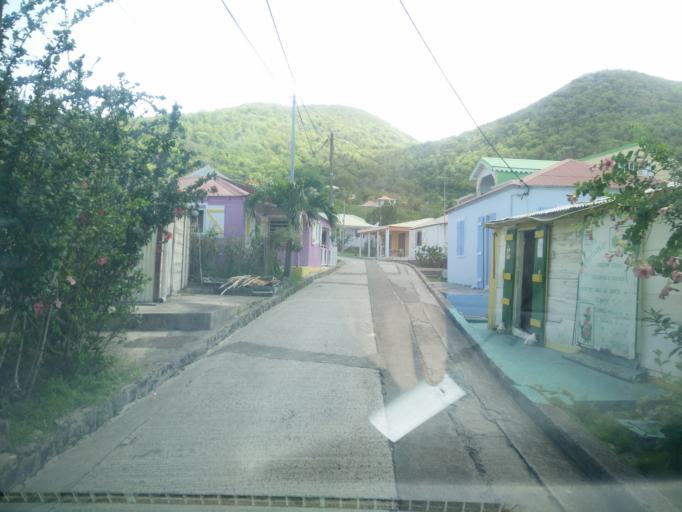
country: GP
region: Guadeloupe
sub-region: Guadeloupe
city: Terre-de-Bas
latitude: 15.8576
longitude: -61.6244
